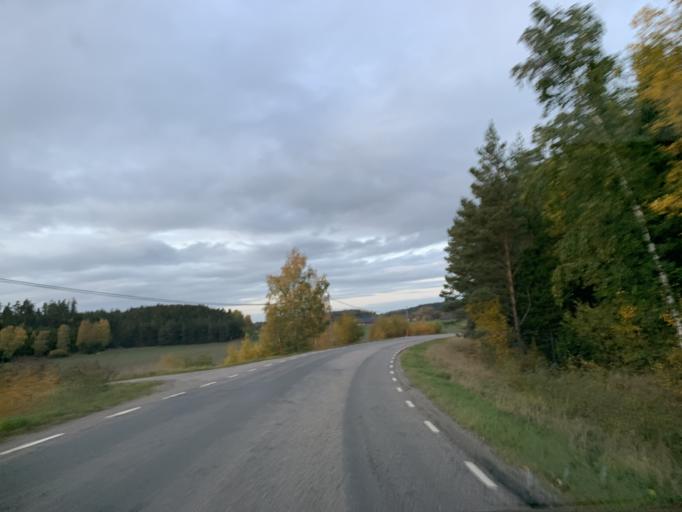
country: SE
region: Stockholm
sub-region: Nynashamns Kommun
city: Osmo
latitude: 58.9474
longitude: 17.7622
